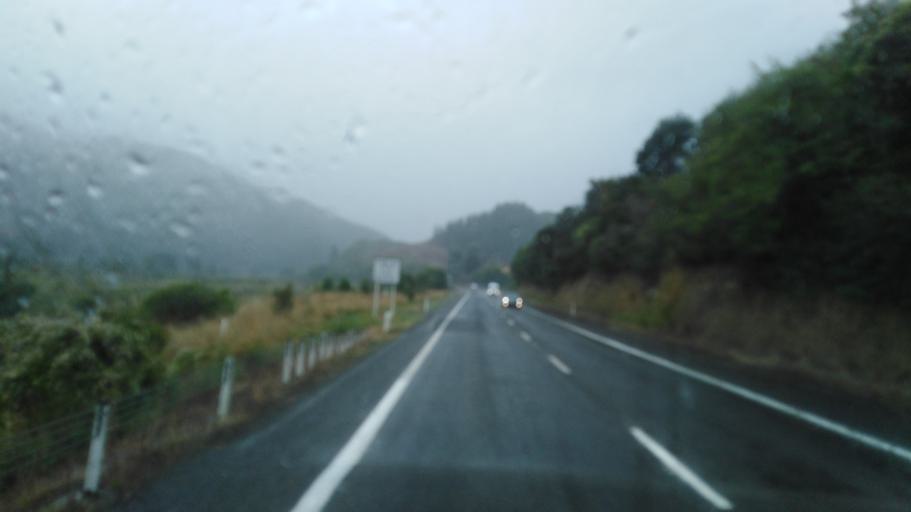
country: NZ
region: Marlborough
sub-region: Marlborough District
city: Blenheim
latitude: -41.4008
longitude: 173.9566
